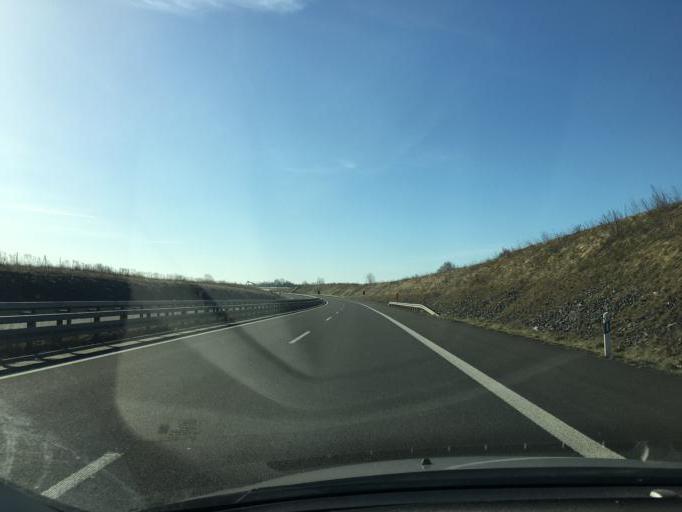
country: DE
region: Saxony
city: Frohburg
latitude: 51.0865
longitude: 12.5358
